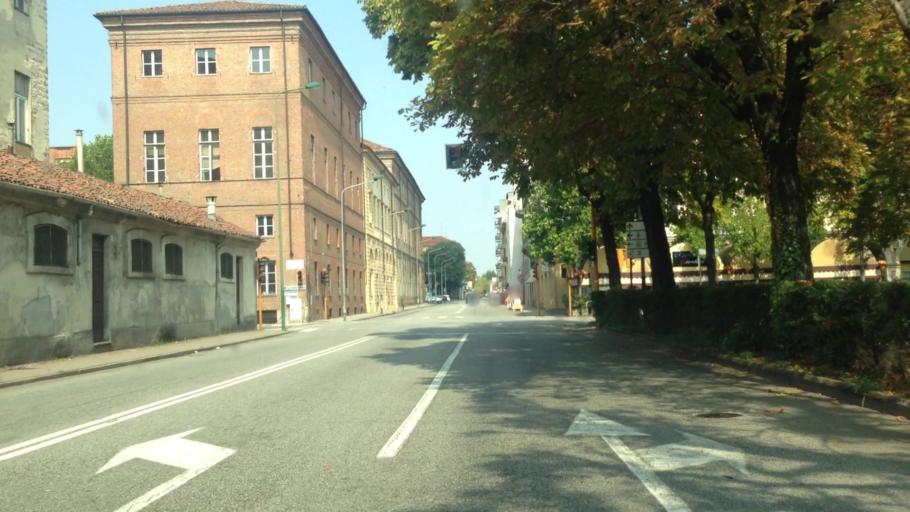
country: IT
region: Piedmont
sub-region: Provincia di Alessandria
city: Casale Monferrato
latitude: 45.1339
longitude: 8.4558
